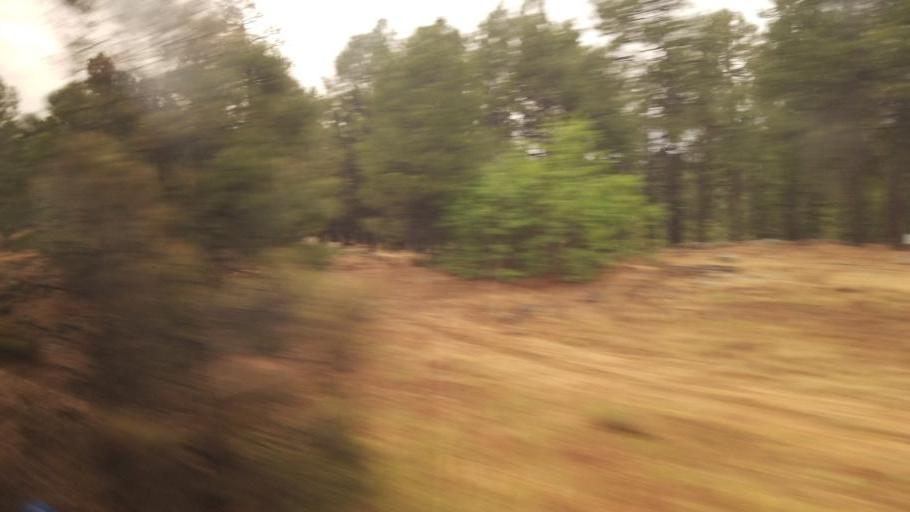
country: US
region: Arizona
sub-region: Coconino County
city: Parks
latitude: 35.2439
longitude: -111.8820
